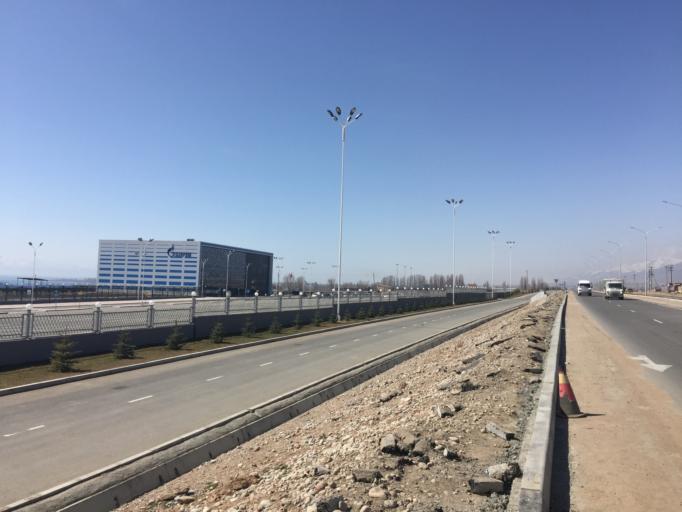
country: KG
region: Ysyk-Koel
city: Cholpon-Ata
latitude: 42.6507
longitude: 77.1248
